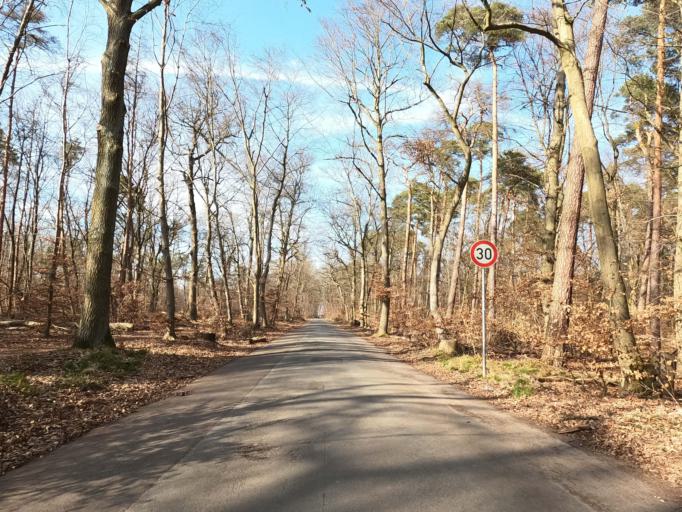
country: DE
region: Hesse
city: Raunheim
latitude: 49.9973
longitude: 8.4588
